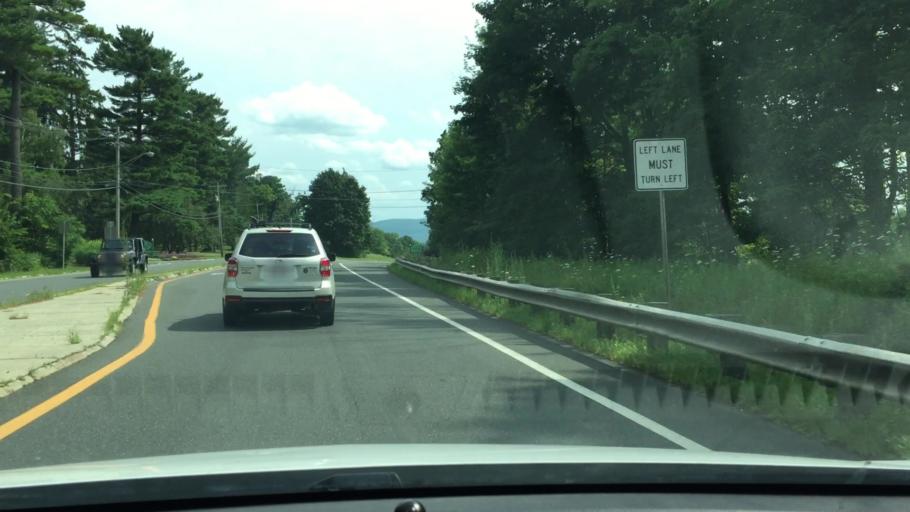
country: US
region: Massachusetts
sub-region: Berkshire County
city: Lenox
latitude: 42.3420
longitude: -73.2696
